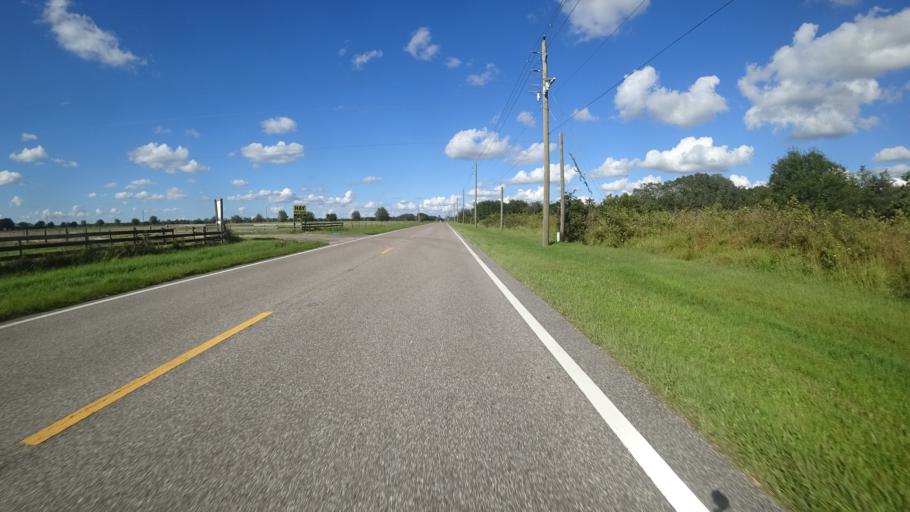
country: US
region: Florida
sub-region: Sarasota County
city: Lake Sarasota
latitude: 27.3697
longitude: -82.2683
